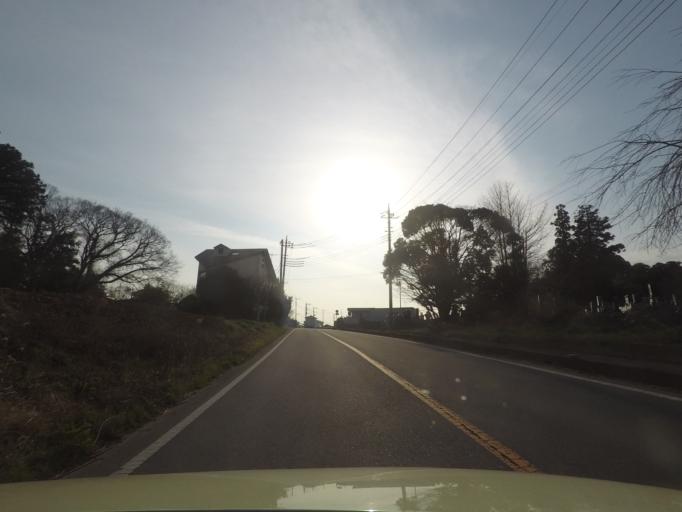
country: JP
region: Ibaraki
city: Okunoya
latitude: 36.2675
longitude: 140.4865
